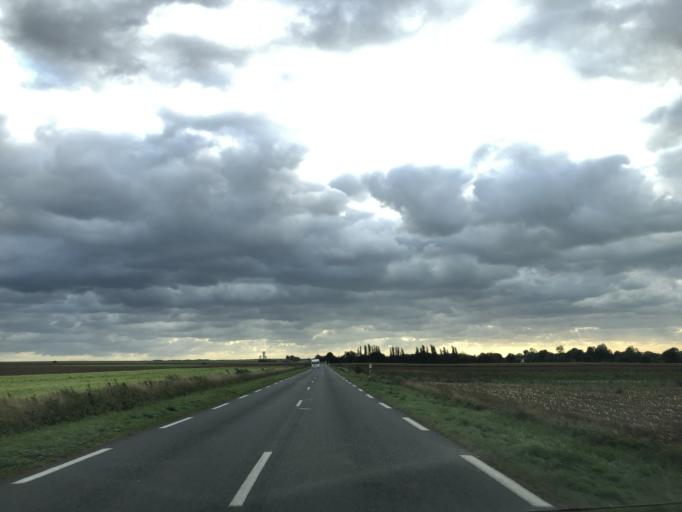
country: FR
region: Picardie
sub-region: Departement de la Somme
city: Pende
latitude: 50.1499
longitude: 1.5443
